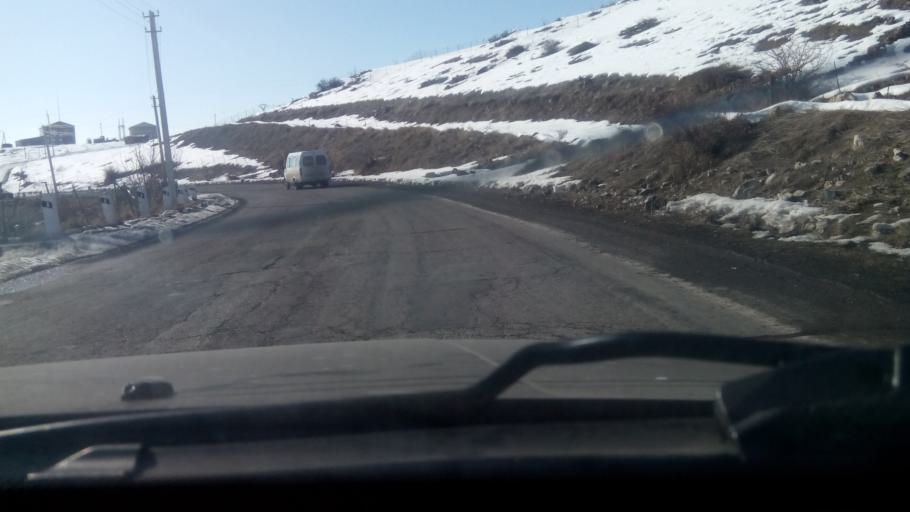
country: AM
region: Kotayk'i Marz
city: Goght'
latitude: 40.1360
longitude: 44.7666
